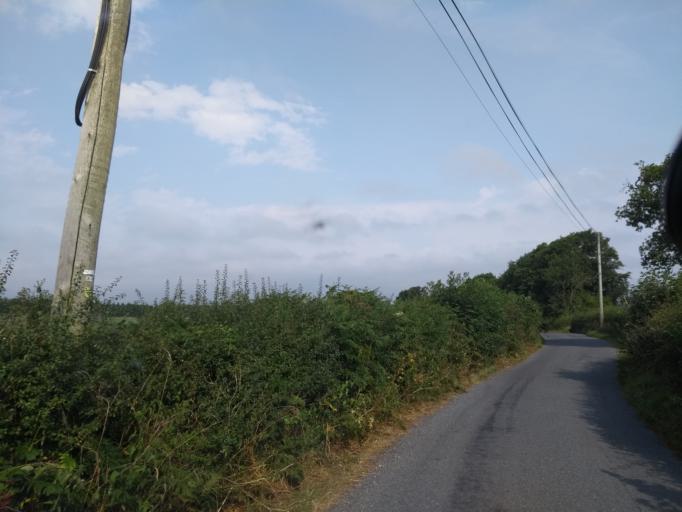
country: GB
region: England
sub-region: Somerset
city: Chard
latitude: 50.8812
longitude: -3.0323
